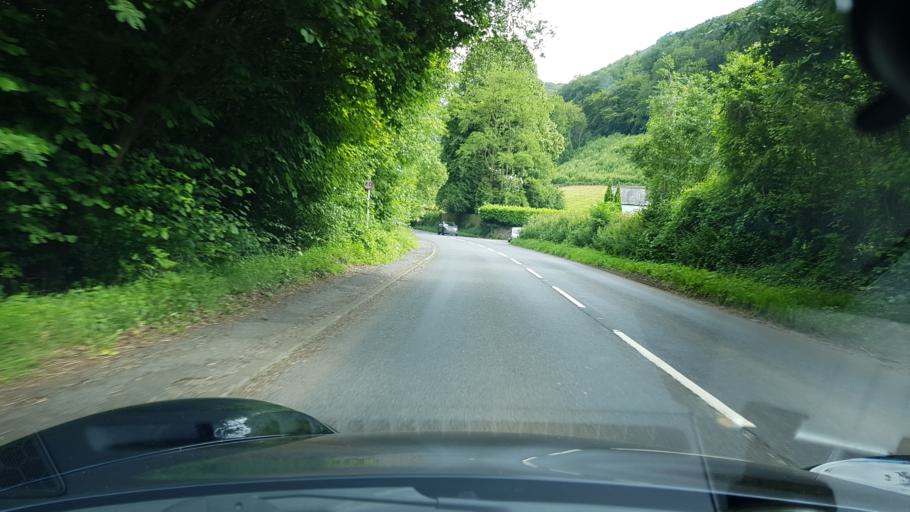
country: GB
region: Wales
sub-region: Monmouthshire
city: Abergavenny
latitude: 51.8167
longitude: -3.0417
